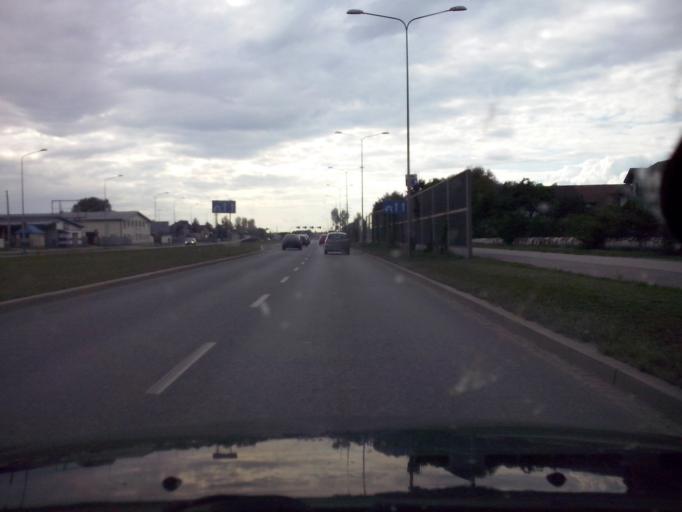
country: PL
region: Lesser Poland Voivodeship
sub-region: Powiat wielicki
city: Czarnochowice
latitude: 50.0387
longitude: 20.0319
